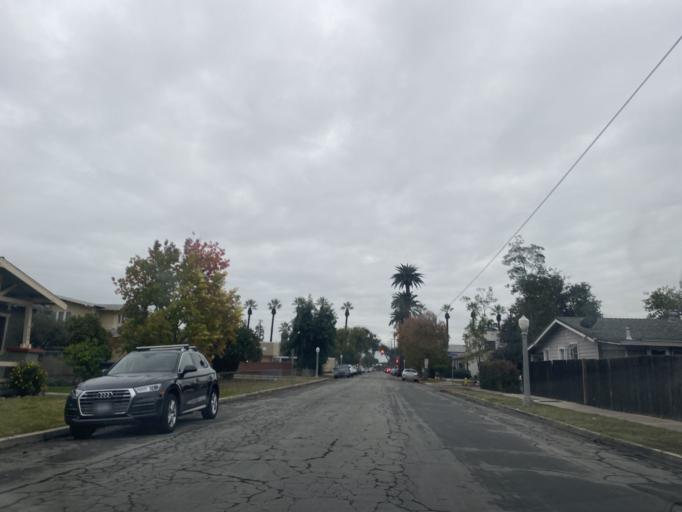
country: US
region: California
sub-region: Orange County
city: Fullerton
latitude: 33.8719
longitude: -117.9156
